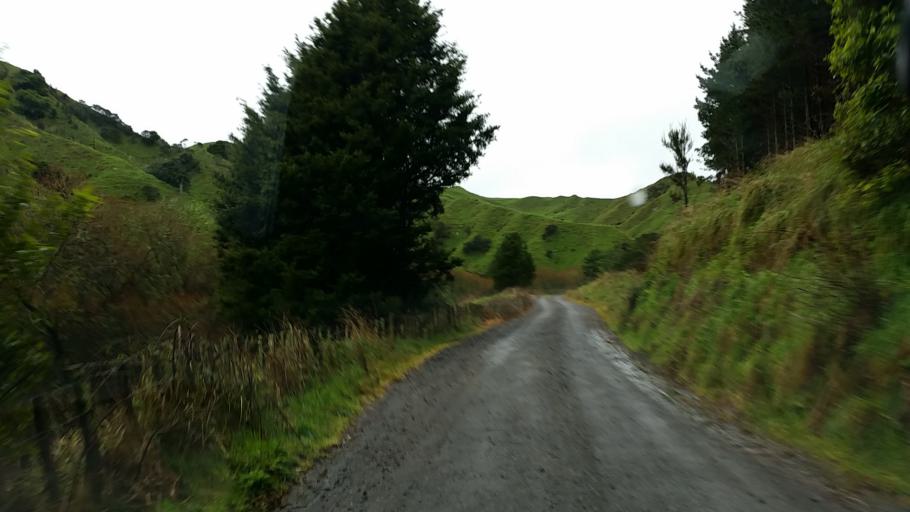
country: NZ
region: Taranaki
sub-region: South Taranaki District
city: Eltham
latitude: -39.5026
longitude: 174.4125
